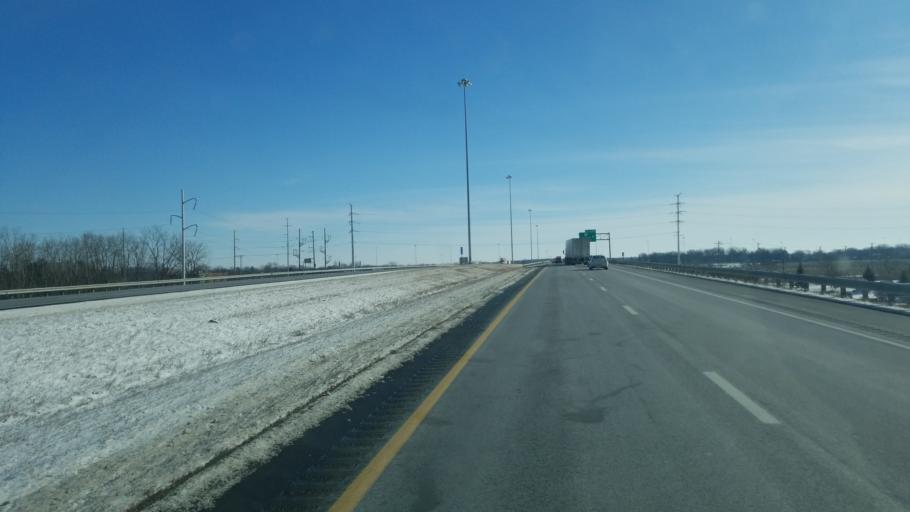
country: US
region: Ohio
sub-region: Lucas County
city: Maumee
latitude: 41.5612
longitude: -83.6889
